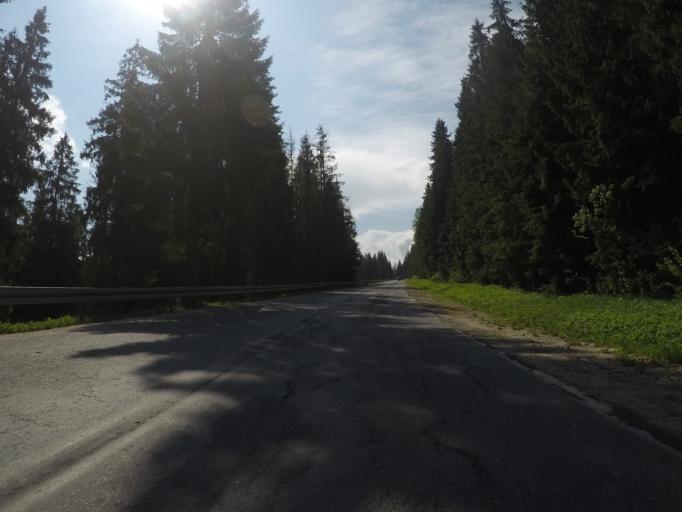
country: PL
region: Lesser Poland Voivodeship
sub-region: Powiat tatrzanski
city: Bukowina Tatrzanska
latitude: 49.3096
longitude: 20.1109
